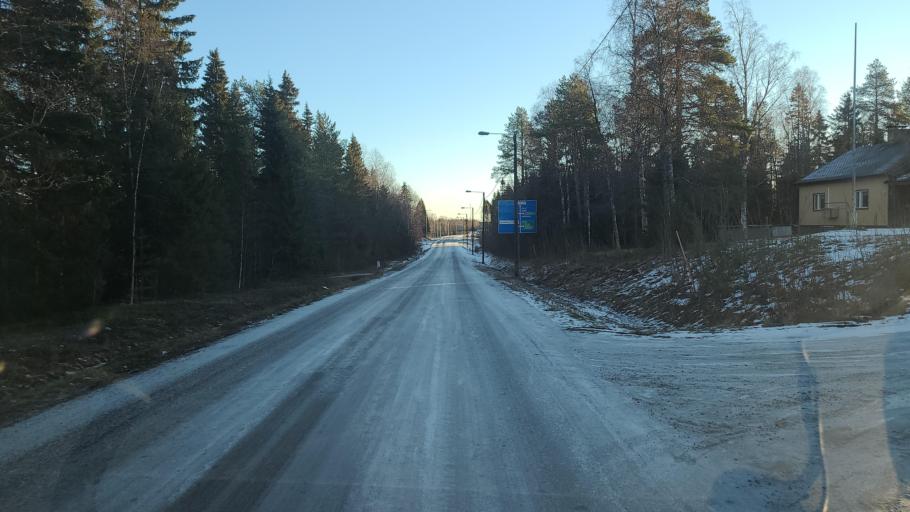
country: FI
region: Lapland
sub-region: Kemi-Tornio
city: Kemi
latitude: 65.6807
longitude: 24.7369
